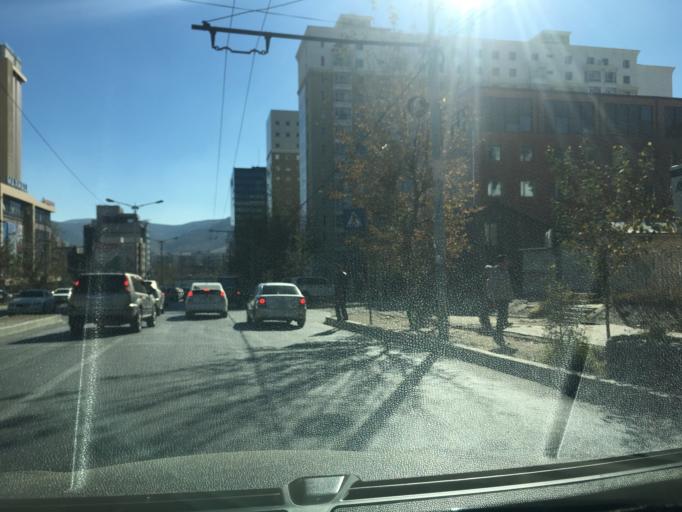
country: MN
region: Ulaanbaatar
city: Ulaanbaatar
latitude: 47.9169
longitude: 106.8909
